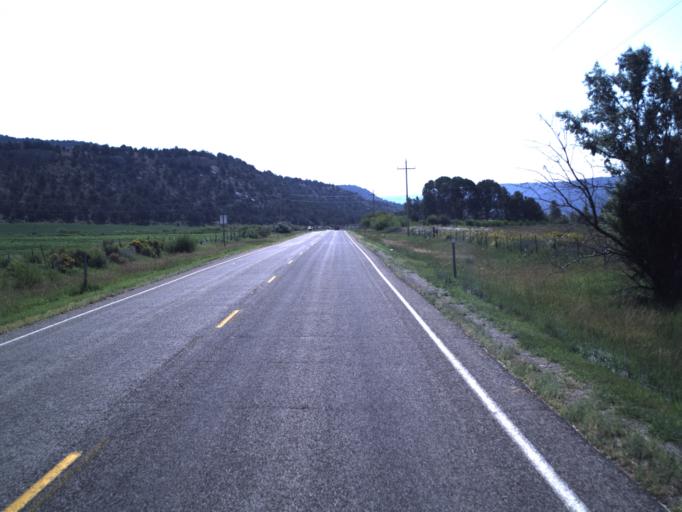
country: US
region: Utah
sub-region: Duchesne County
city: Duchesne
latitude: 40.3347
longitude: -110.6783
